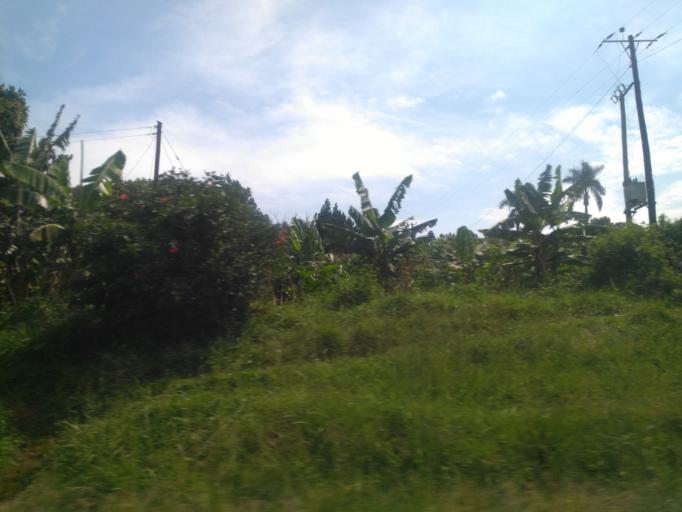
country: UG
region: Central Region
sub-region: Wakiso District
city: Entebbe
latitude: 0.0486
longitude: 32.4568
